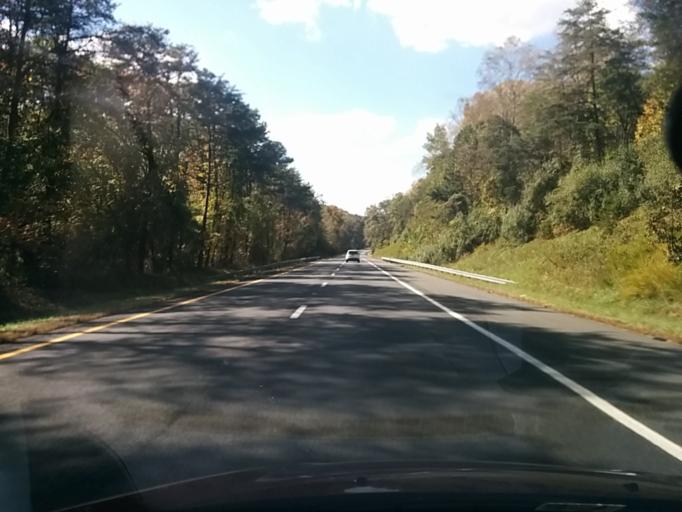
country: US
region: Virginia
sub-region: Albemarle County
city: Crozet
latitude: 38.0313
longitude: -78.6519
